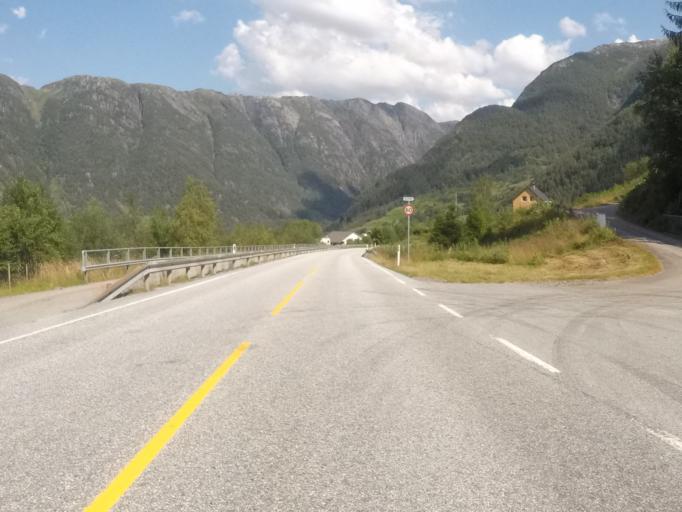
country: NO
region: Hordaland
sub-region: Masfjorden
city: Masfjorden
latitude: 60.8995
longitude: 5.5216
